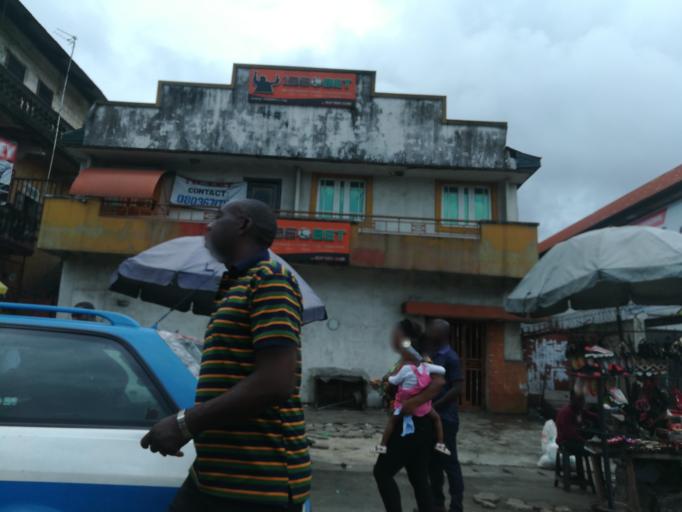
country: NG
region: Rivers
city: Port Harcourt
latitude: 4.7615
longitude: 7.0192
